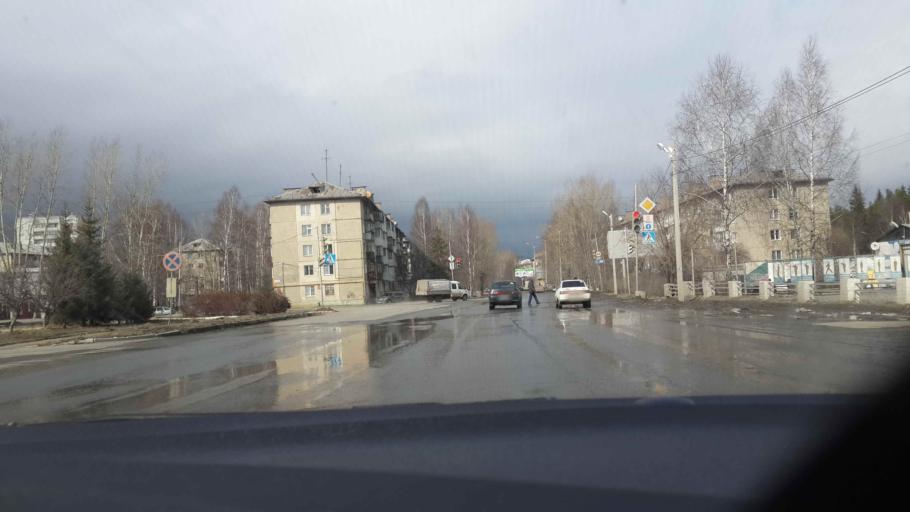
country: RU
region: Chelyabinsk
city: Zlatoust
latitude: 55.1399
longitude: 59.6739
